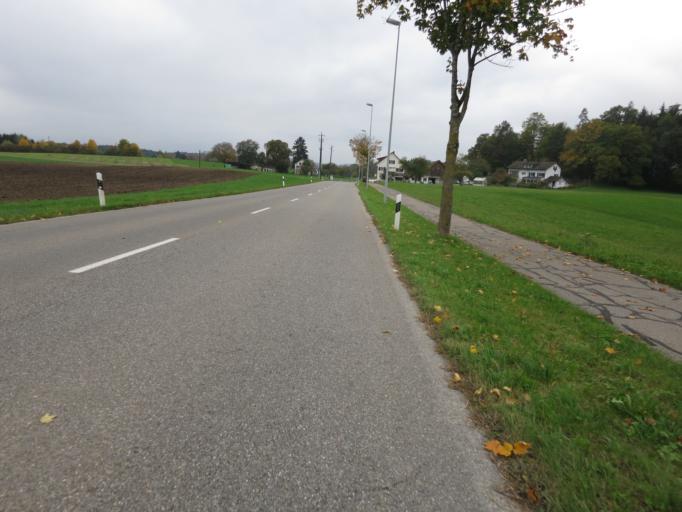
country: CH
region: Zurich
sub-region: Bezirk Hinwil
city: Bubikon
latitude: 47.2844
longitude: 8.7987
